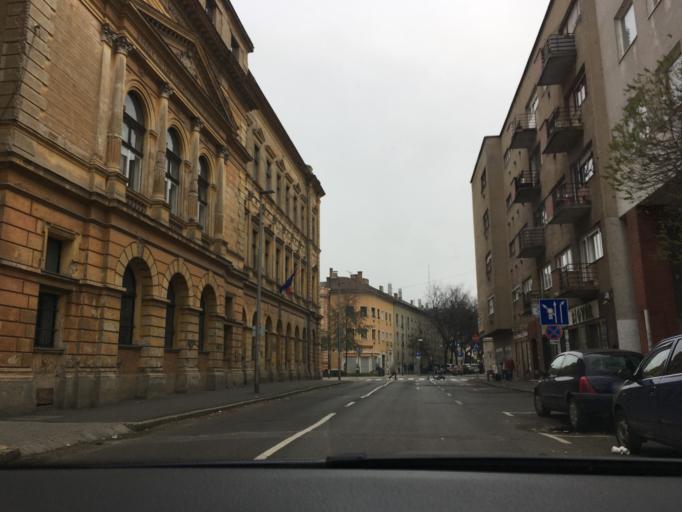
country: HU
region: Hajdu-Bihar
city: Debrecen
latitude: 47.5320
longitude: 21.6272
